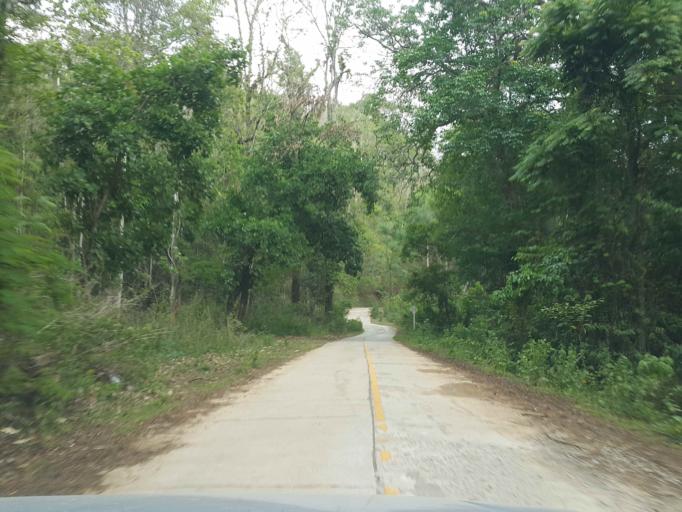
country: TH
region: Chiang Mai
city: Wiang Haeng
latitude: 19.3788
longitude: 98.7486
